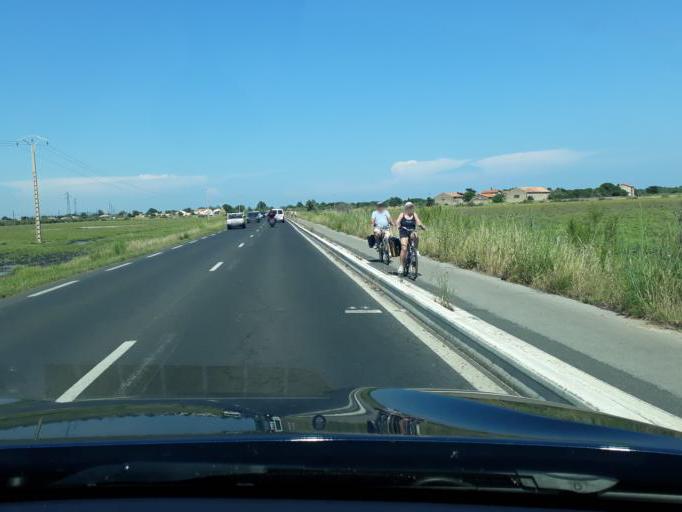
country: FR
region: Languedoc-Roussillon
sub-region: Departement de l'Herault
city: Le Cap d'Agde
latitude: 43.3119
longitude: 3.5228
